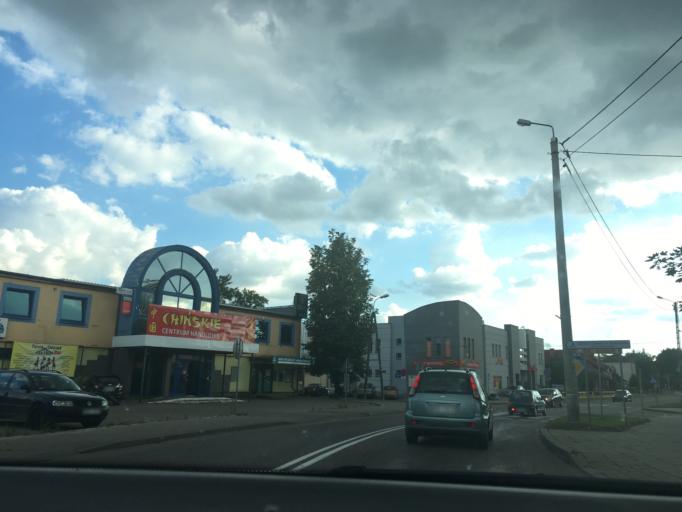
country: PL
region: Podlasie
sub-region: Powiat bielski
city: Bielsk Podlaski
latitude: 52.7634
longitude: 23.1858
